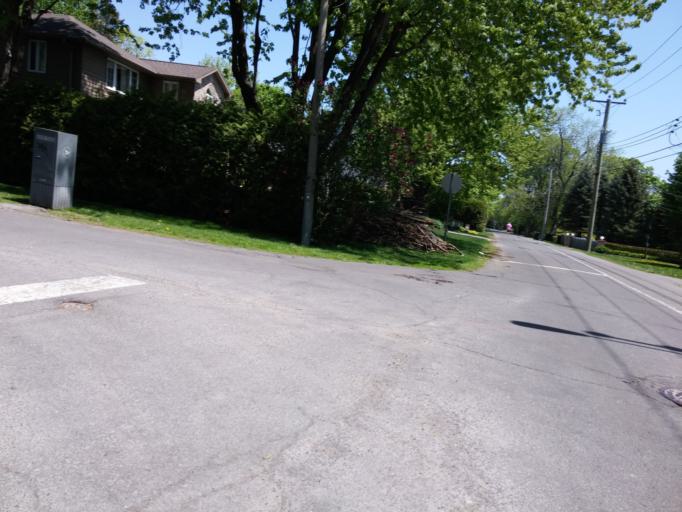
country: CA
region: Quebec
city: Baie-D'Urfe
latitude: 45.4149
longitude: -73.8926
